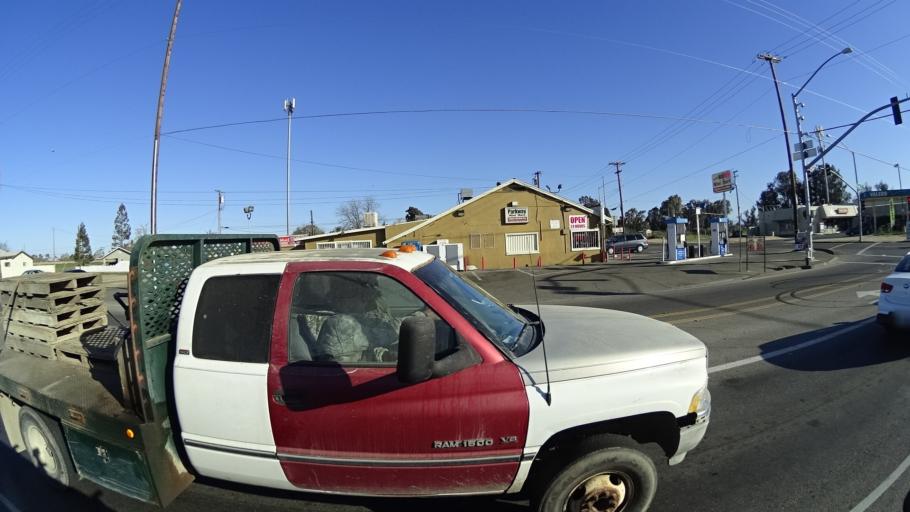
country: US
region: California
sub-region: Fresno County
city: West Park
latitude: 36.8080
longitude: -119.8898
